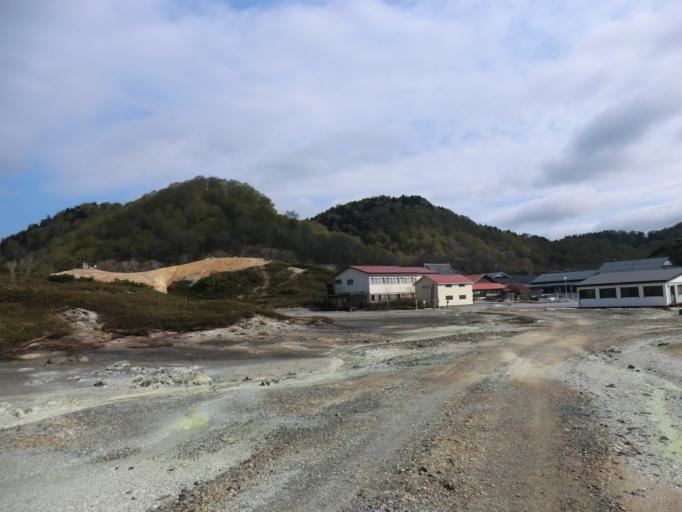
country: JP
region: Aomori
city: Mutsu
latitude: 41.3259
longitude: 141.0897
